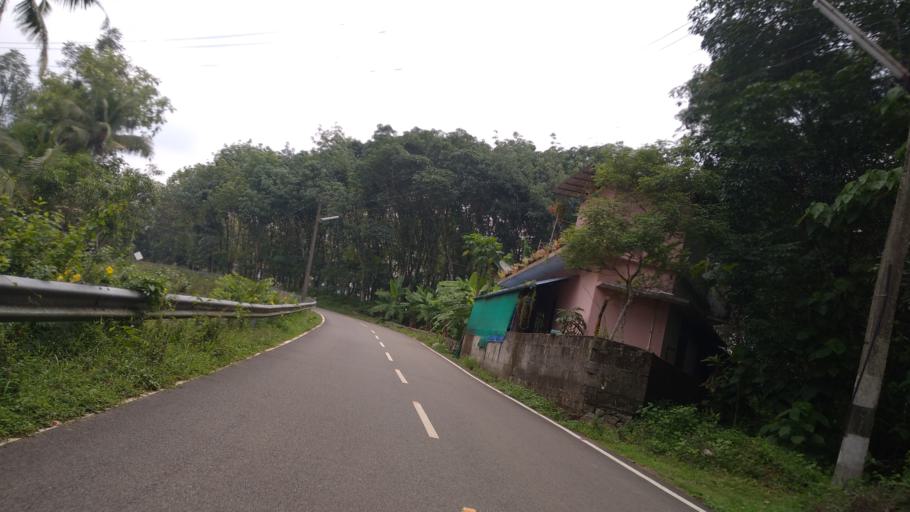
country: IN
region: Kerala
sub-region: Ernakulam
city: Perumbavoor
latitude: 10.0219
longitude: 76.4864
